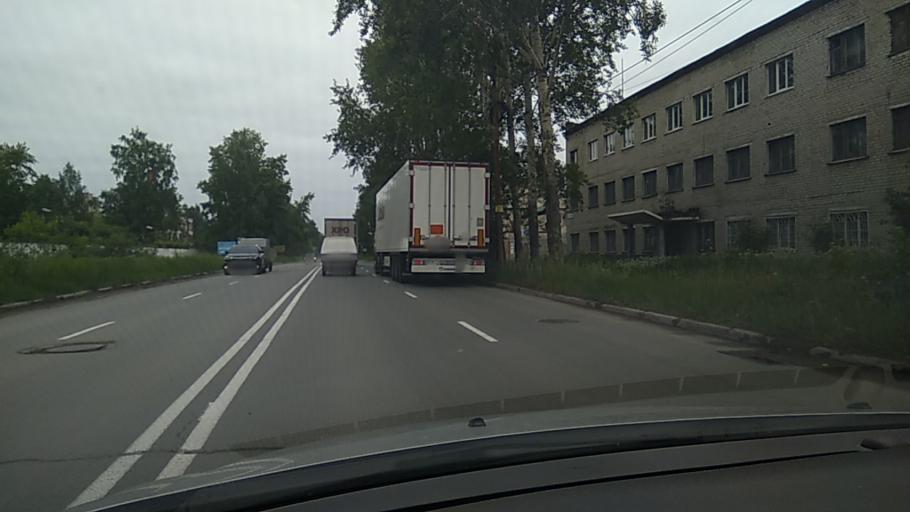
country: RU
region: Sverdlovsk
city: Shuvakish
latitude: 56.8887
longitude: 60.5241
